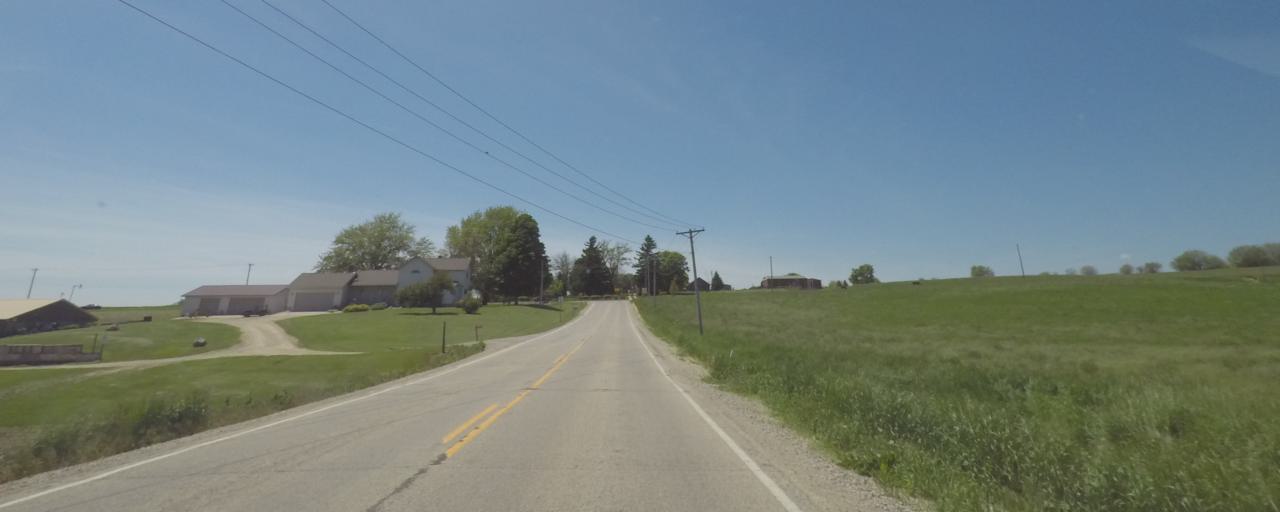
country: US
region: Wisconsin
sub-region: Green County
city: Brooklyn
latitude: 42.7872
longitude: -89.3670
